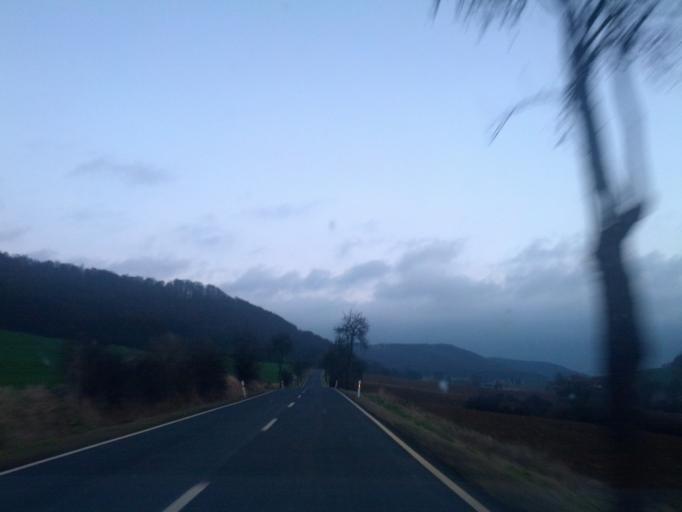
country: DE
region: Thuringia
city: Ifta
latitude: 51.0922
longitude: 10.2162
